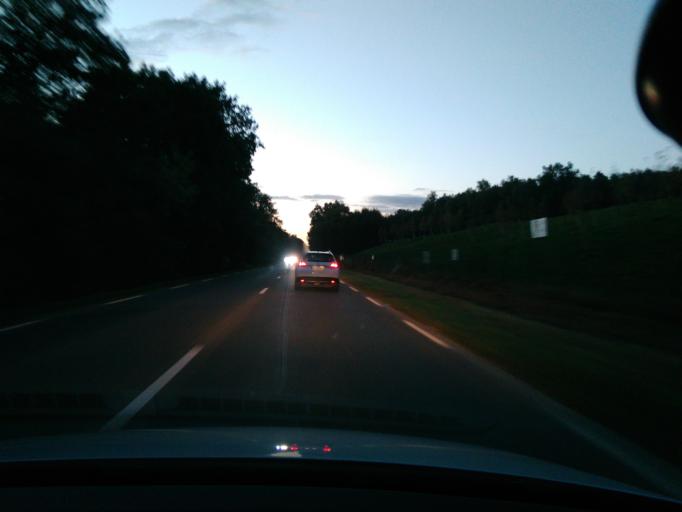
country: FR
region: Ile-de-France
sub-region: Departement de Seine-et-Marne
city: Villeneuve-le-Comte
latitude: 48.8243
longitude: 2.8099
